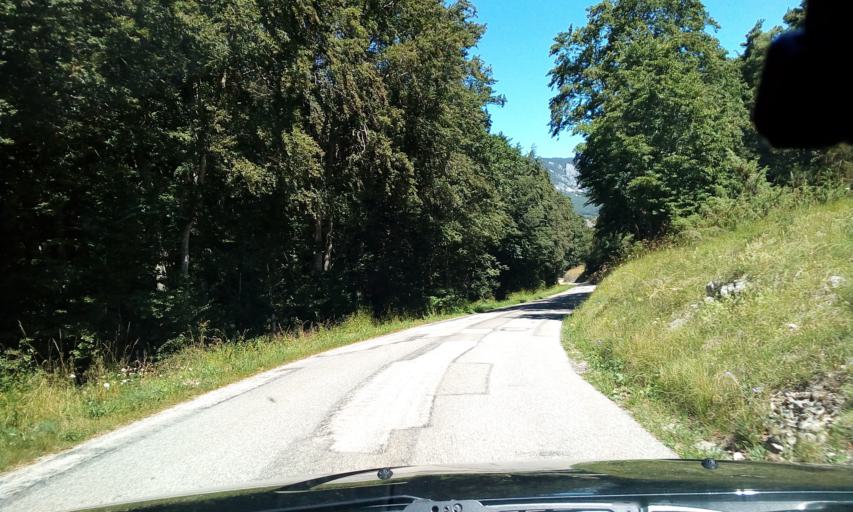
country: FR
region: Rhone-Alpes
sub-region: Departement de la Drome
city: Die
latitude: 44.8783
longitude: 5.3635
